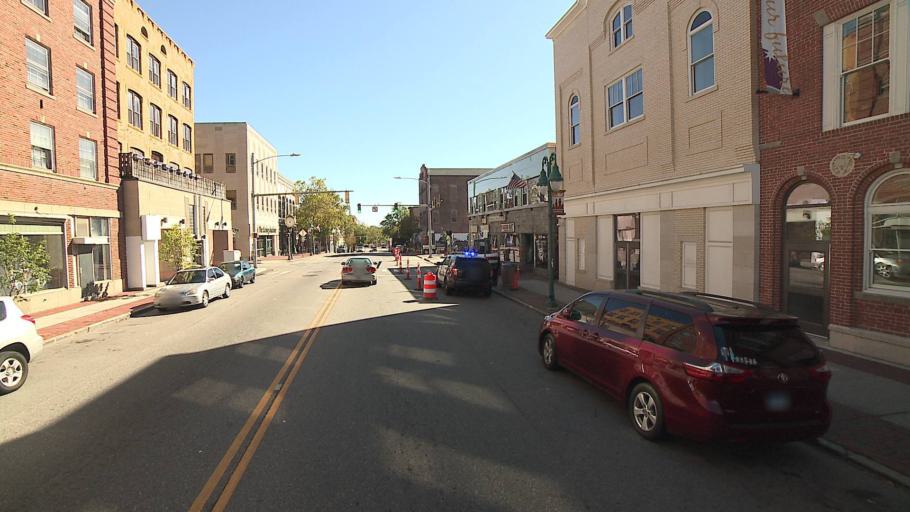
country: US
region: Connecticut
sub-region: Windham County
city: Willimantic
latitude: 41.7124
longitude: -72.2148
